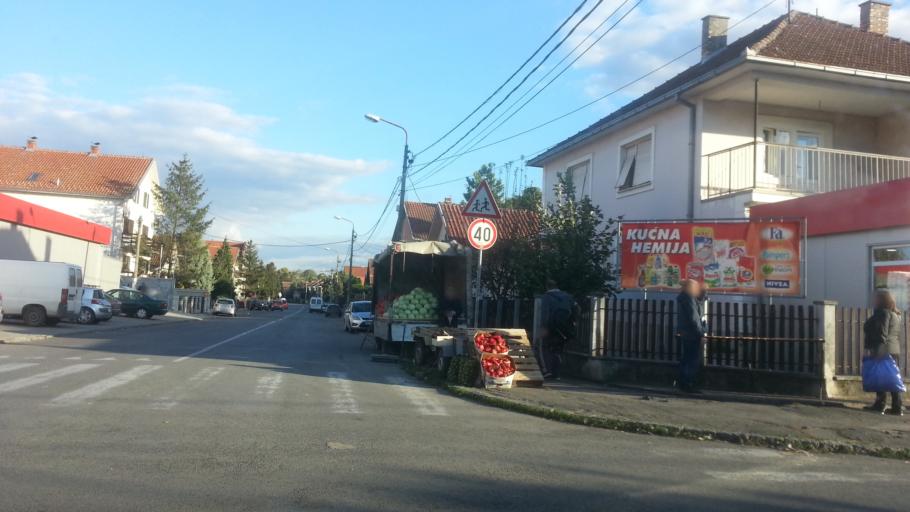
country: RS
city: Novi Banovci
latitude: 44.9043
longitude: 20.2837
